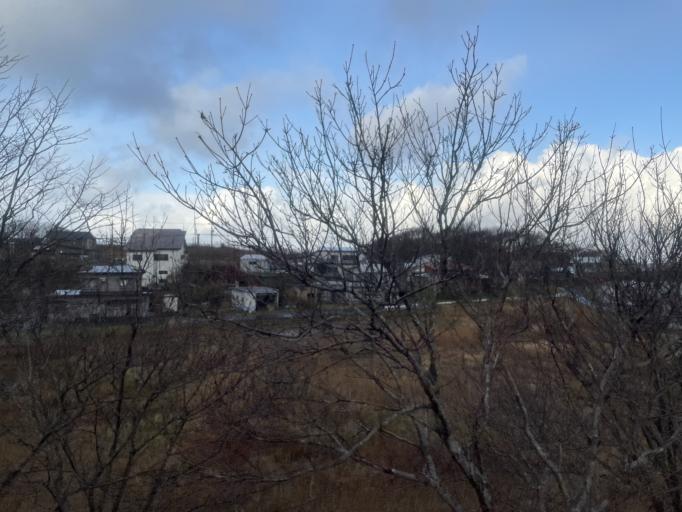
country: JP
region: Aomori
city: Misawa
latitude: 40.9189
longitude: 141.1935
